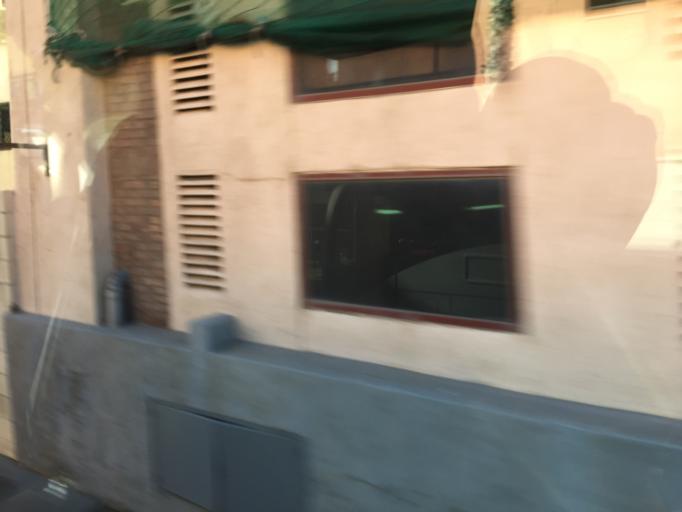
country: ES
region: Catalonia
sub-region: Provincia de Barcelona
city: Ciutat Vella
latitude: 41.3712
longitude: 2.1876
